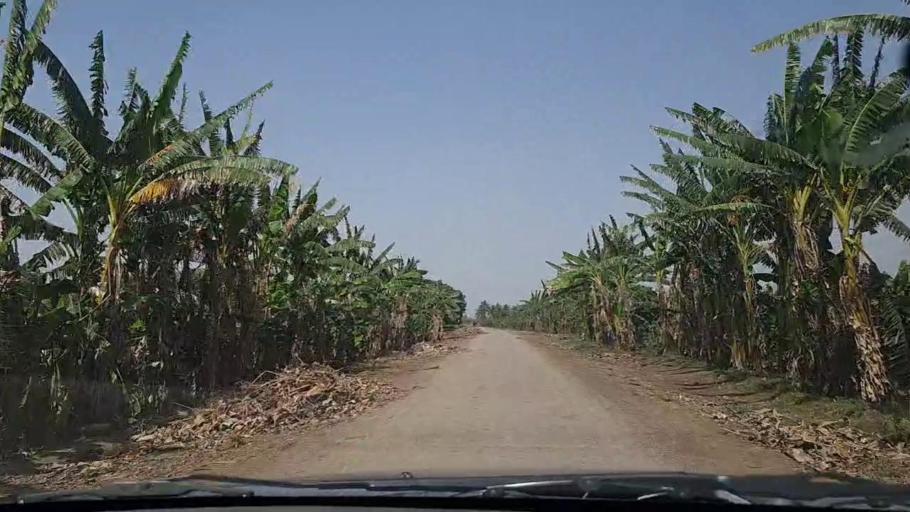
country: PK
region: Sindh
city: Keti Bandar
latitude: 24.2803
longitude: 67.6720
